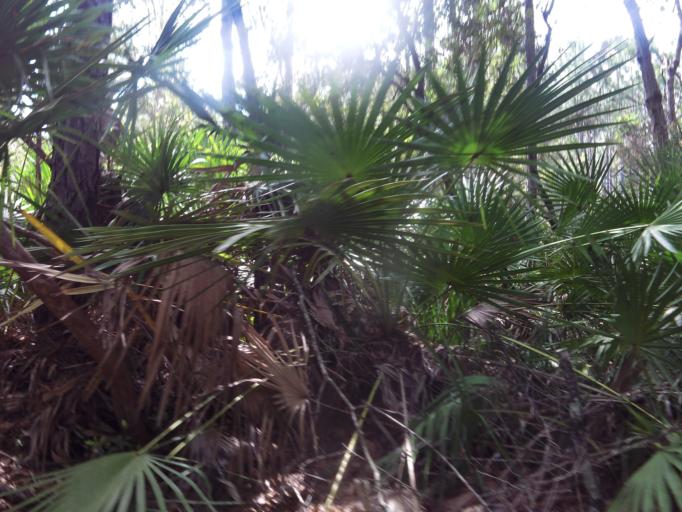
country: US
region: Florida
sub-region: Duval County
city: Atlantic Beach
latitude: 30.4534
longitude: -81.4742
